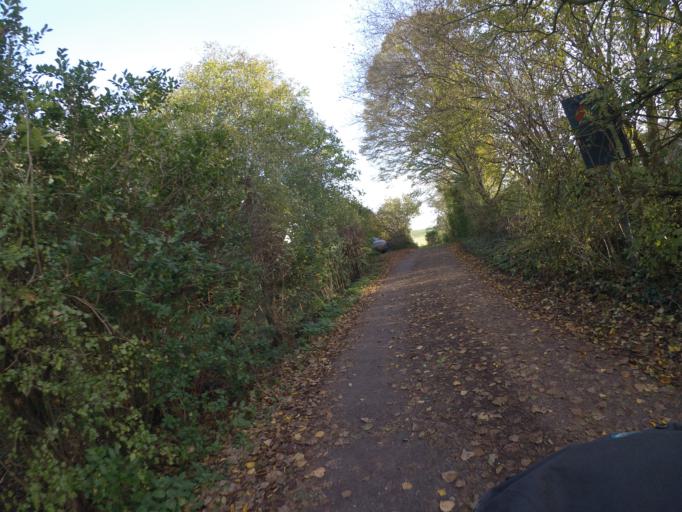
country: NL
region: Gelderland
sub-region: Gemeente Maasdriel
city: Heerewaarden
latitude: 51.8326
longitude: 5.3969
